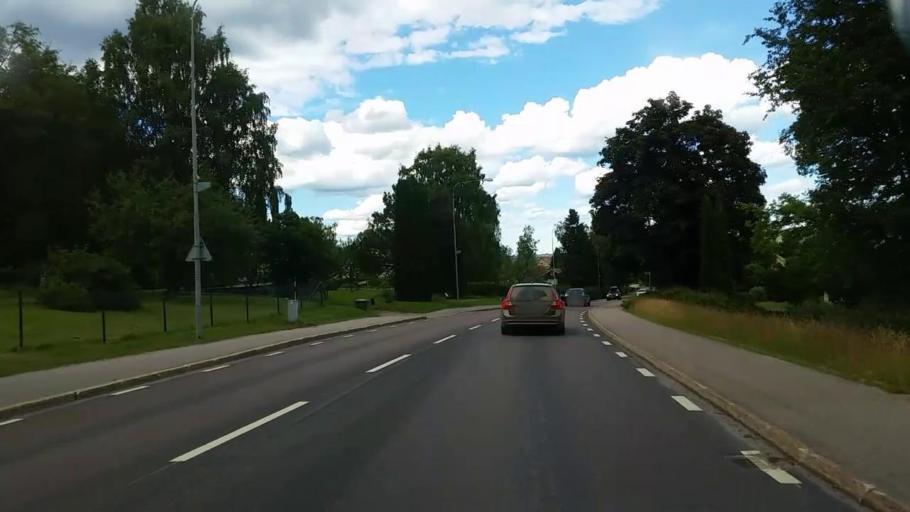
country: SE
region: Gaevleborg
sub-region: Ljusdals Kommun
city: Jaervsoe
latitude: 61.7094
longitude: 16.1647
